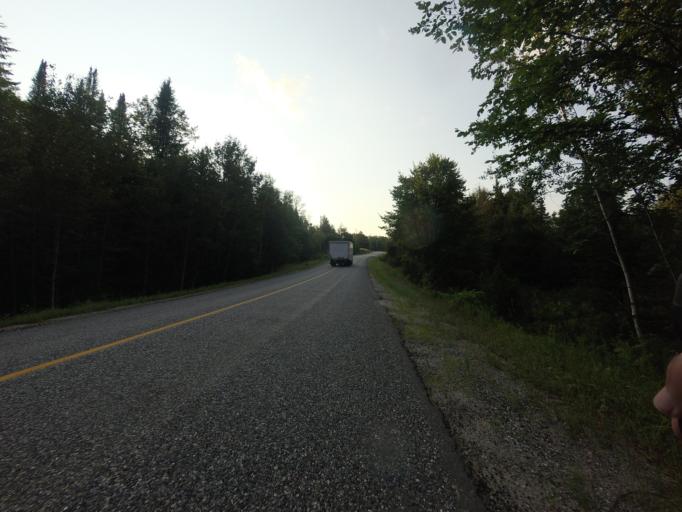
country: CA
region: Ontario
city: Renfrew
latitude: 45.0167
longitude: -76.7637
